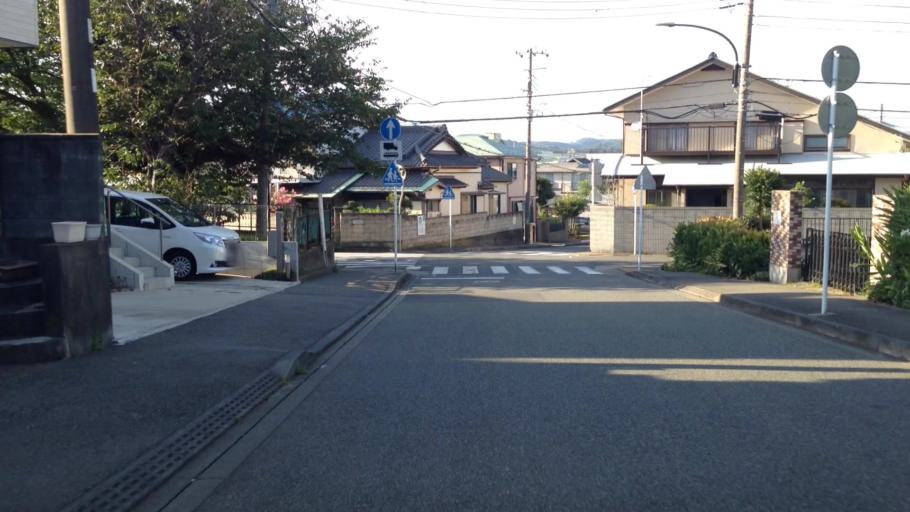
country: JP
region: Kanagawa
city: Miura
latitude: 35.2065
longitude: 139.6154
